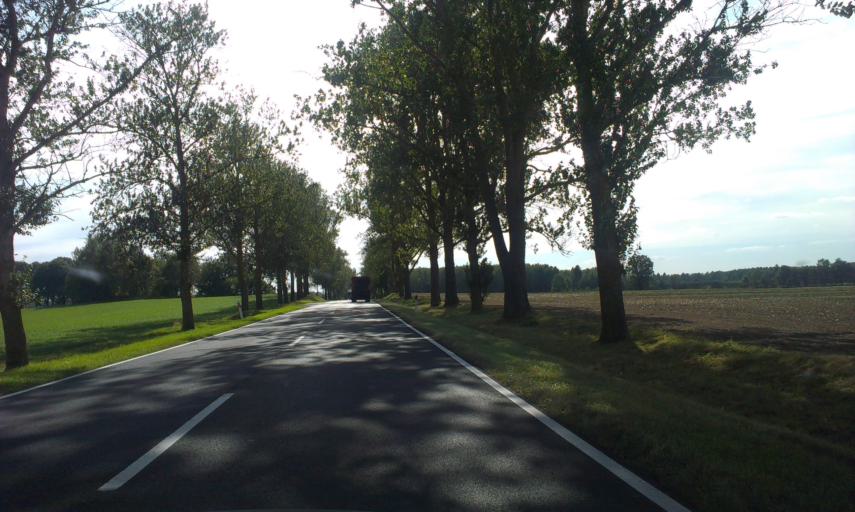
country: PL
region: Greater Poland Voivodeship
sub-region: Powiat zlotowski
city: Okonek
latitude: 53.5933
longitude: 16.8157
